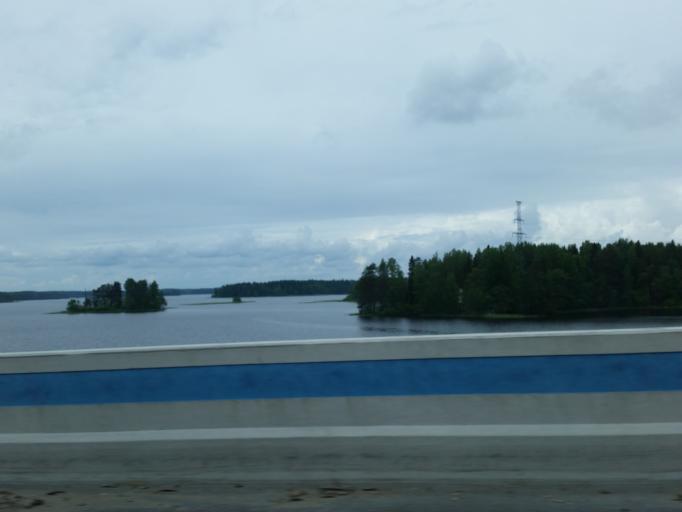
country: FI
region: Northern Savo
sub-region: Kuopio
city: Kuopio
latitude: 62.9454
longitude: 27.6697
